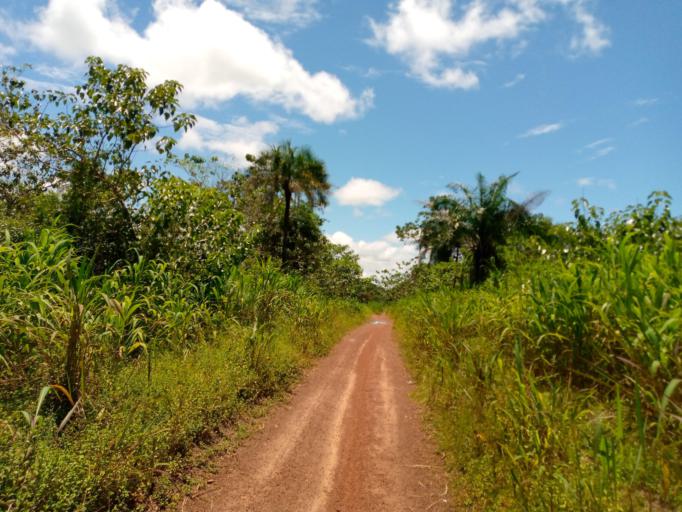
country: SL
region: Northern Province
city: Makeni
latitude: 9.0429
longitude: -12.1579
